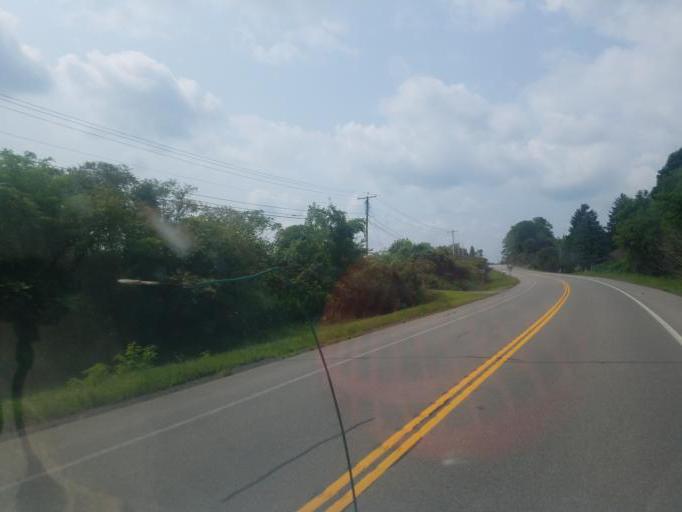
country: US
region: New York
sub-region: Herkimer County
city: Herkimer
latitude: 43.0185
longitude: -74.9636
